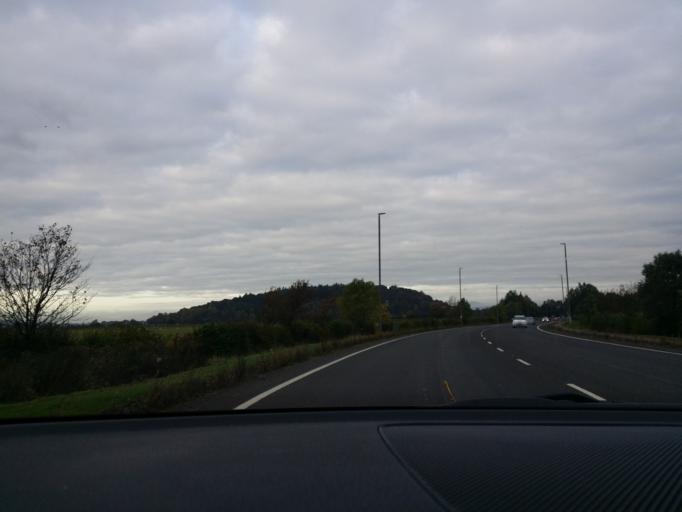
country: GB
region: Scotland
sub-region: Stirling
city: Stirling
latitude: 56.1251
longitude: -3.9569
